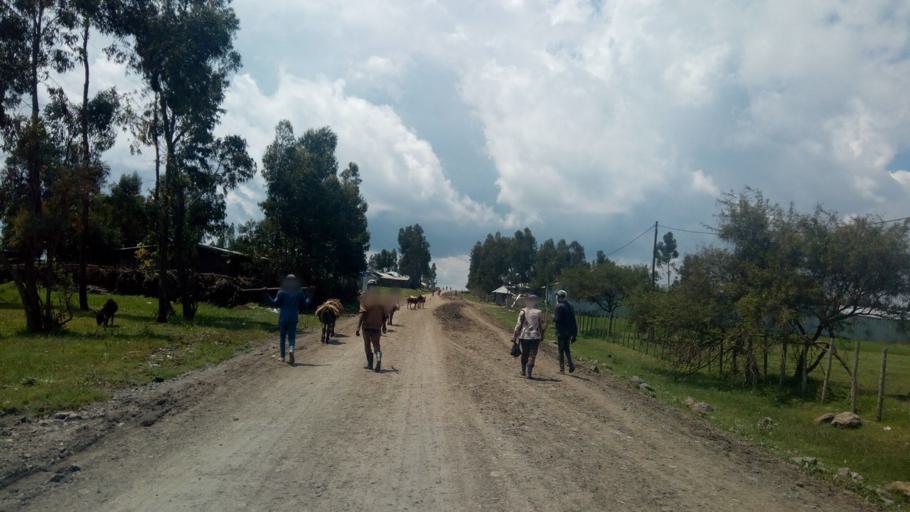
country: ET
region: Oromiya
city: Sendafa
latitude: 8.9993
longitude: 39.1272
